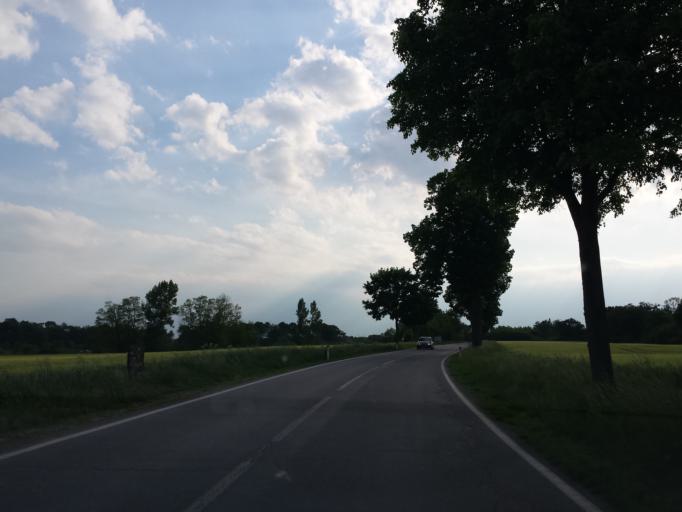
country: AT
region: Lower Austria
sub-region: Politischer Bezirk Ganserndorf
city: Marchegg
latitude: 48.2765
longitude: 16.8952
